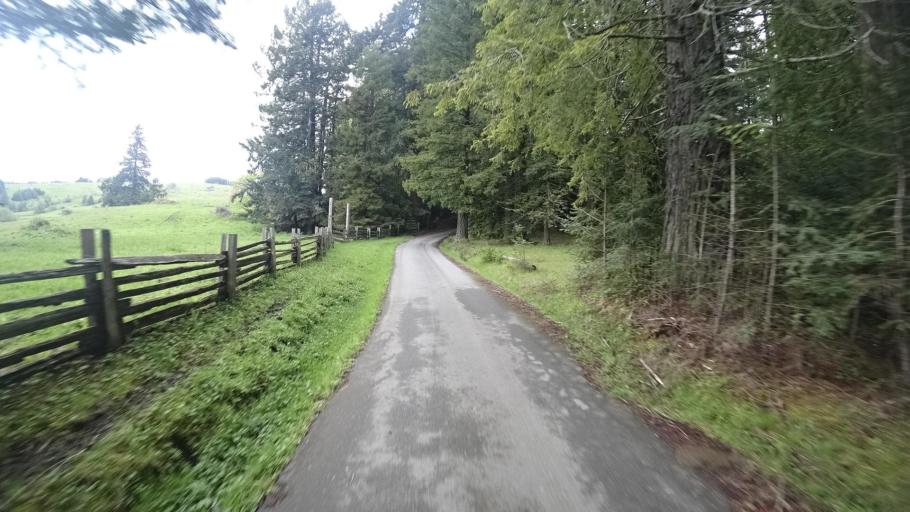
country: US
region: California
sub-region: Humboldt County
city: Blue Lake
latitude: 40.9086
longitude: -123.9655
